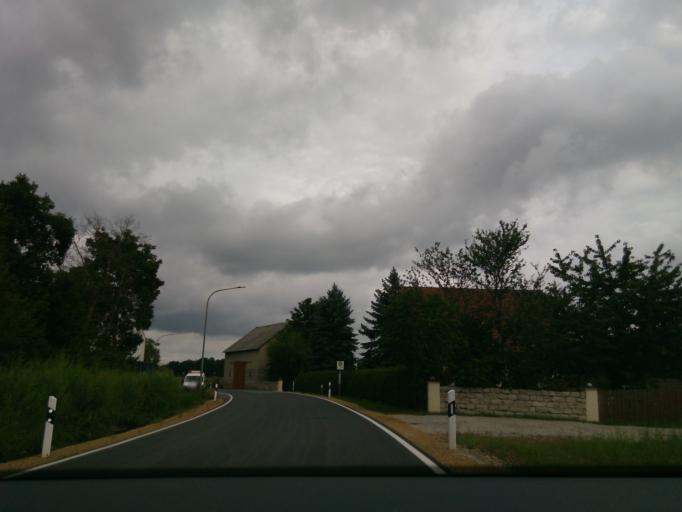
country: DE
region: Bavaria
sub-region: Regierungsbezirk Mittelfranken
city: Gremsdorf
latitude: 49.6755
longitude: 10.8084
